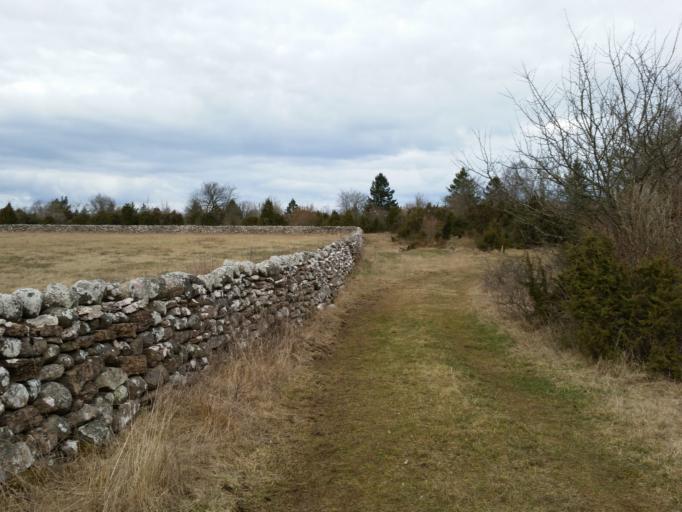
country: SE
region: Kalmar
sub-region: Morbylanga Kommun
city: Sodra Sandby
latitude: 56.6751
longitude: 16.5806
